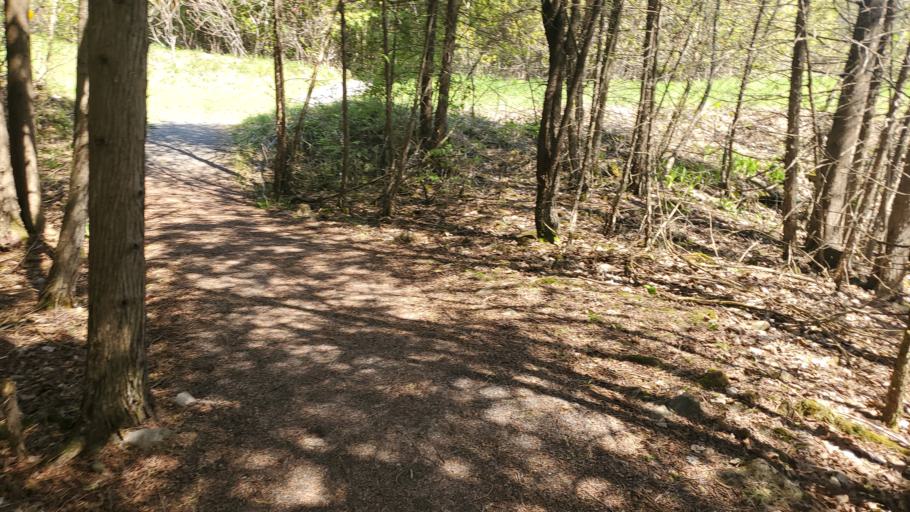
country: CA
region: Ontario
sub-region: Lanark County
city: Smiths Falls
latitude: 44.9126
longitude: -75.8285
